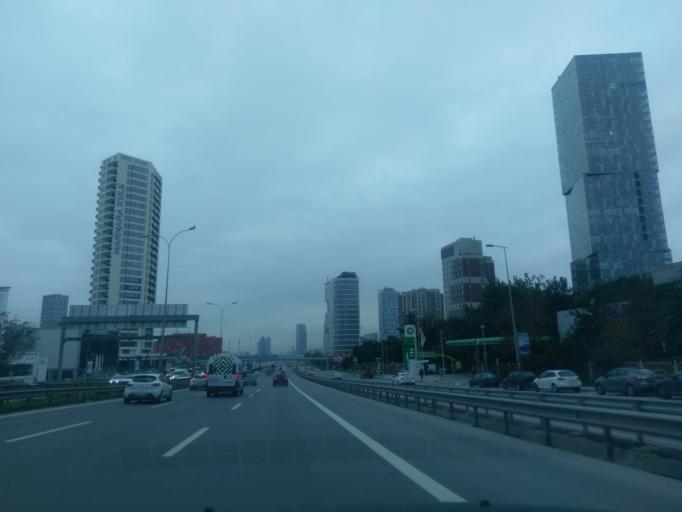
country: TR
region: Istanbul
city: Maltepe
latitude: 40.9102
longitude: 29.2000
